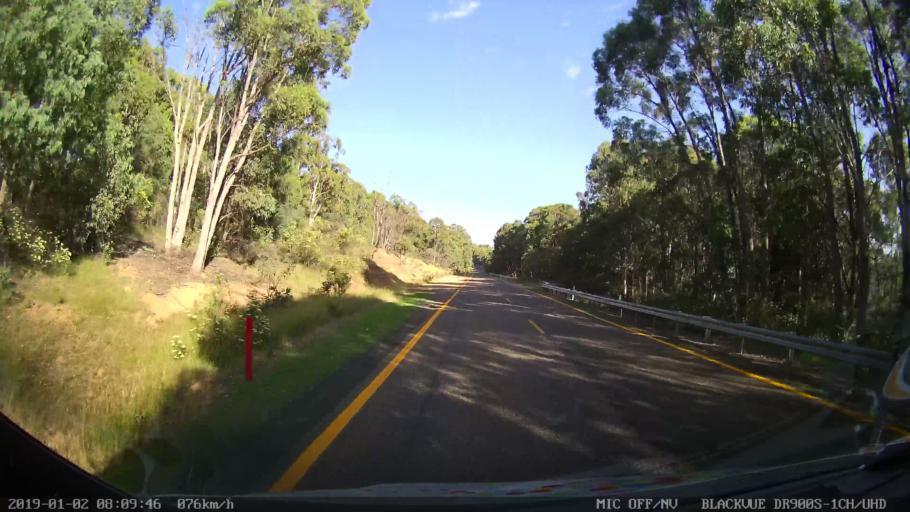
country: AU
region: New South Wales
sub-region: Tumut Shire
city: Tumut
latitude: -35.6040
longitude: 148.3767
